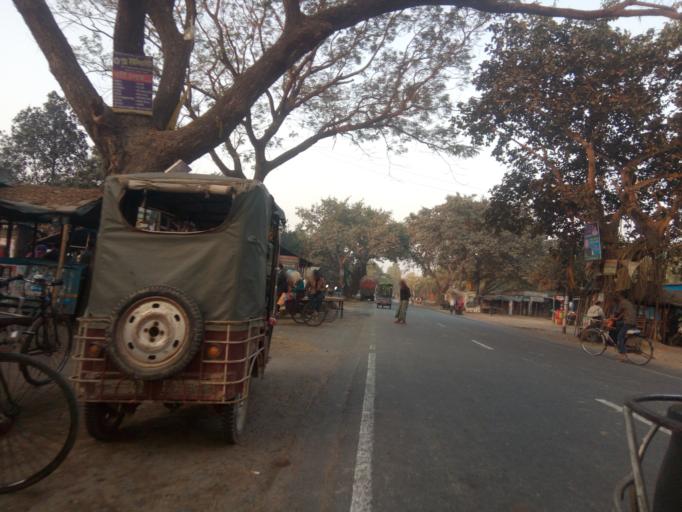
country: BD
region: Rajshahi
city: Bogra
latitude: 24.6272
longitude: 89.2436
